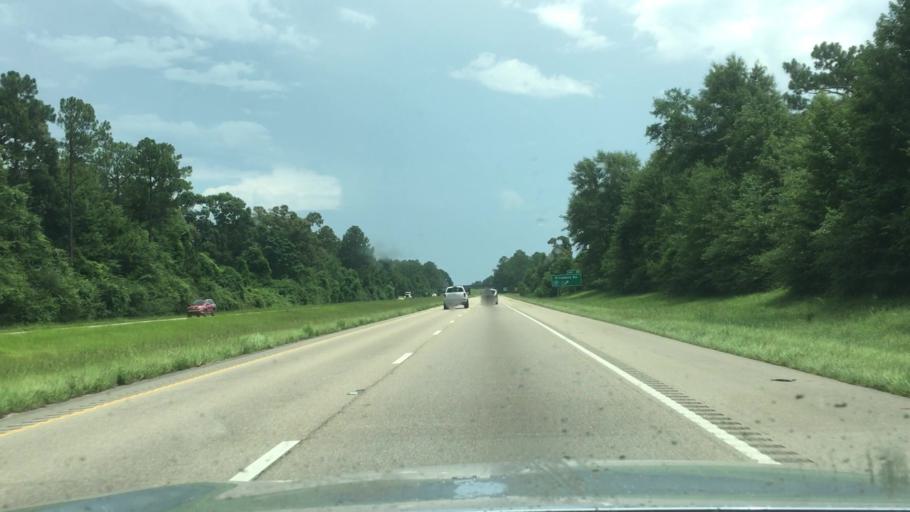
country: US
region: Mississippi
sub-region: Lamar County
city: Lumberton
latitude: 30.9187
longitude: -89.4612
